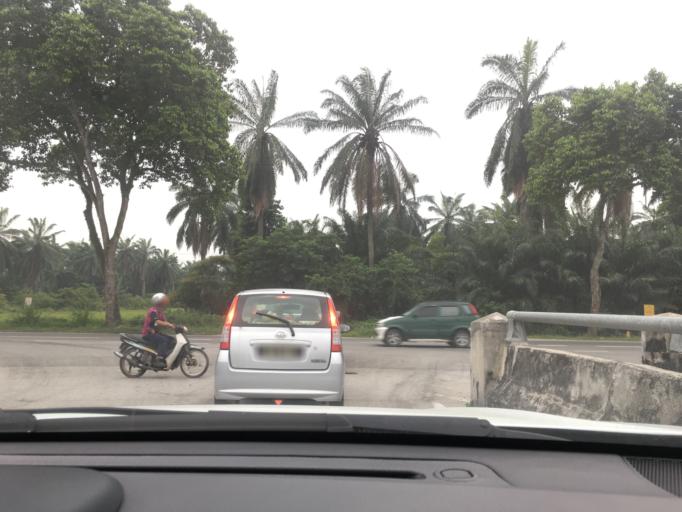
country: MY
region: Selangor
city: Klang
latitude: 3.1364
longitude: 101.4055
